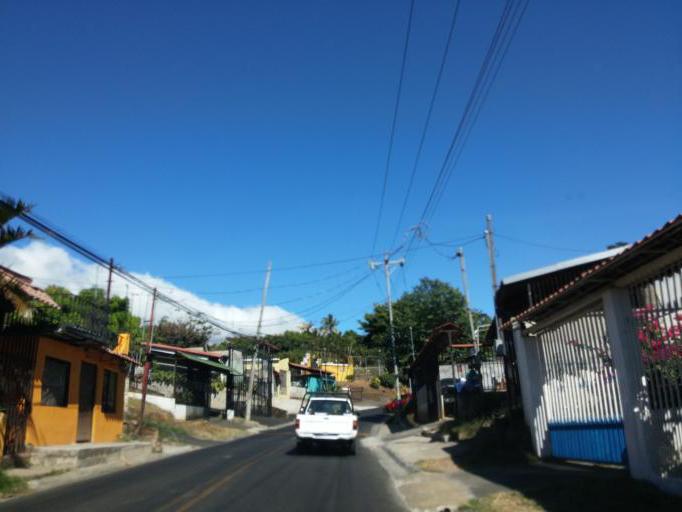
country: CR
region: Alajuela
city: Alajuela
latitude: 10.0198
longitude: -84.1852
